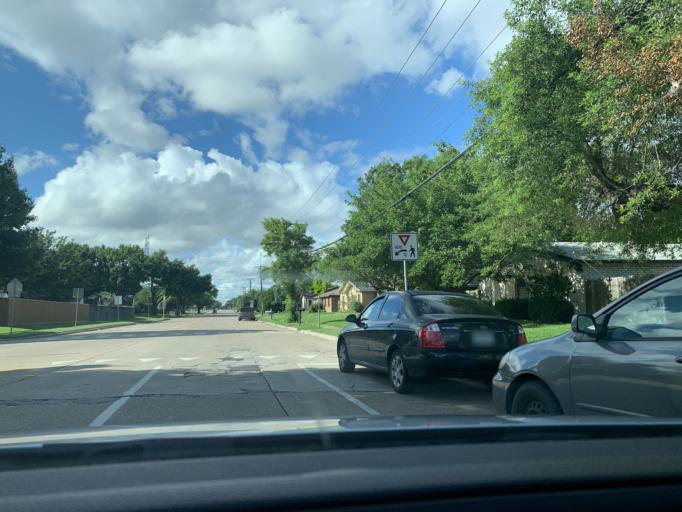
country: US
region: Texas
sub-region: Dallas County
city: Grand Prairie
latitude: 32.6543
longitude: -97.0278
